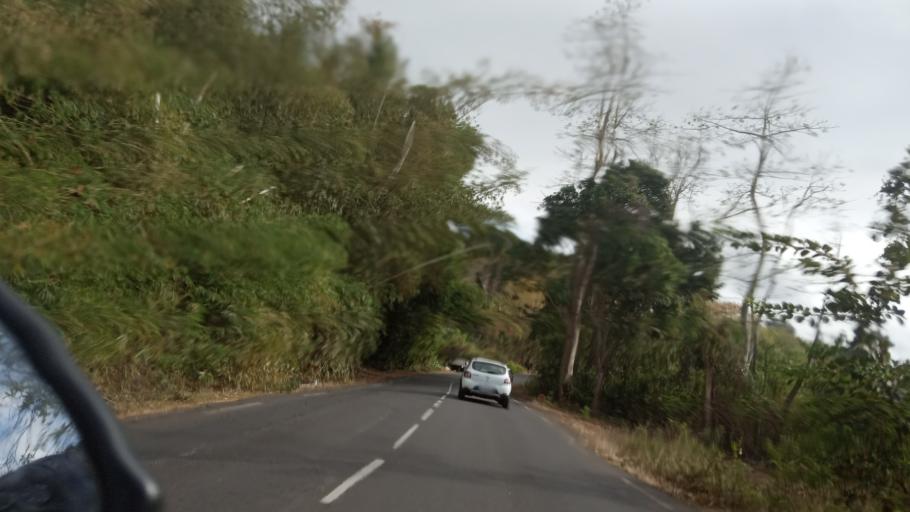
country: YT
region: Dembeni
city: Dembeni
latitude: -12.8252
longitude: 45.1941
